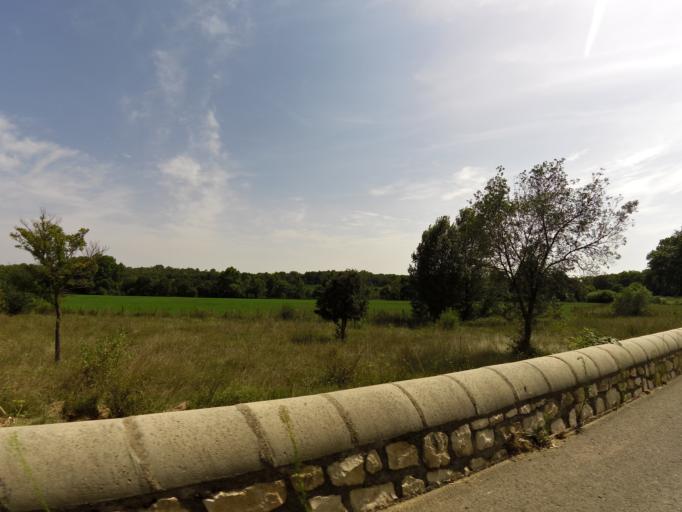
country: FR
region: Languedoc-Roussillon
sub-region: Departement du Gard
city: Villevieille
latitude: 43.8136
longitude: 4.0951
